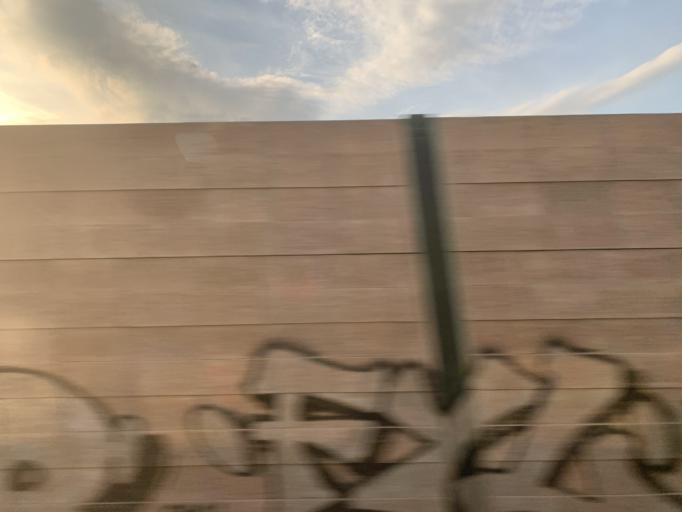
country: ES
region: Catalonia
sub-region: Provincia de Girona
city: Breda
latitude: 41.7268
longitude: 2.5688
